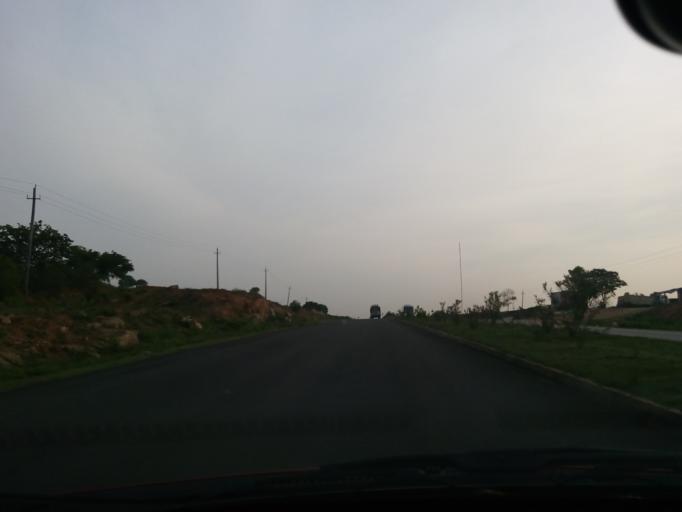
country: IN
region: Karnataka
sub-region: Chikkaballapur
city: Gudibanda
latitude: 13.6061
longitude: 77.7876
